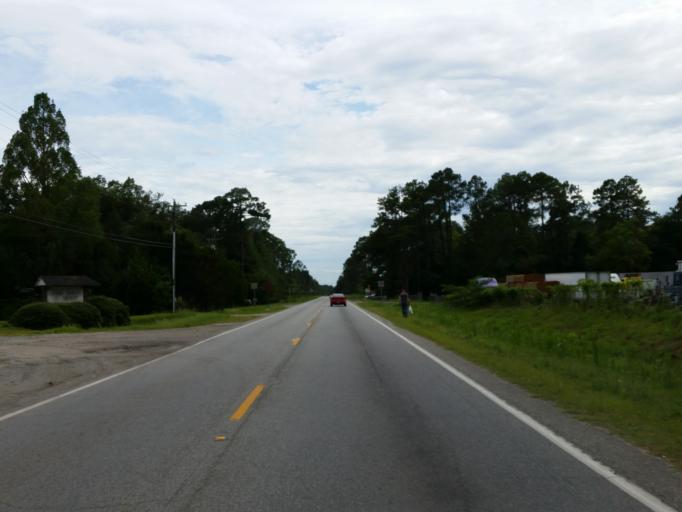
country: US
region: Georgia
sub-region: Lowndes County
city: Valdosta
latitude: 30.7446
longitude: -83.2769
